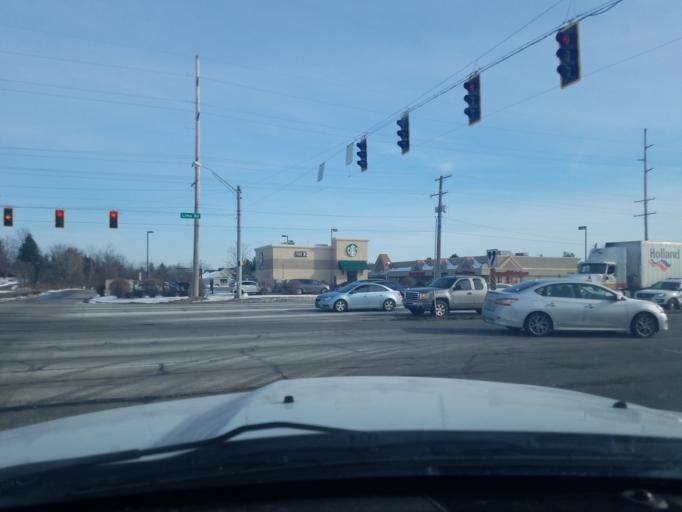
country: US
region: Indiana
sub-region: Allen County
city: Huntertown
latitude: 41.1750
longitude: -85.1662
